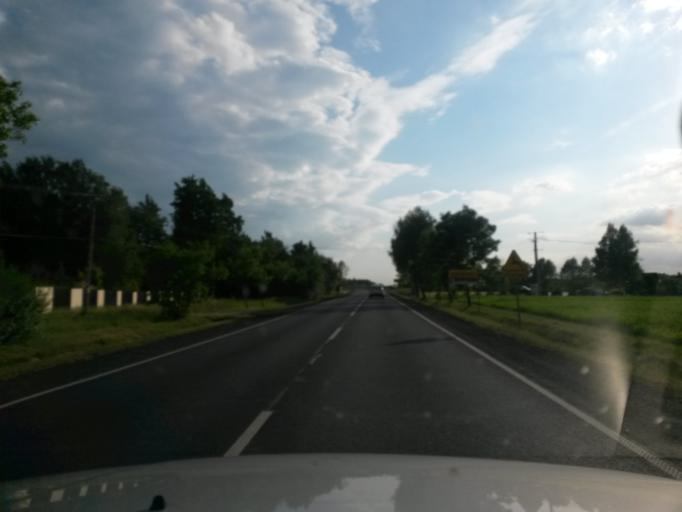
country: PL
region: Lodz Voivodeship
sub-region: Powiat belchatowski
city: Belchatow
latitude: 51.3951
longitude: 19.4160
